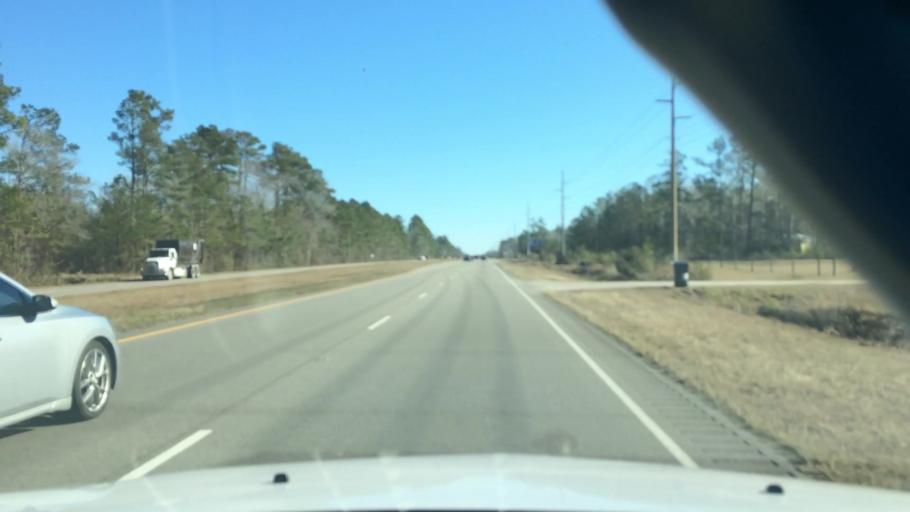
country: US
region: North Carolina
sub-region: Brunswick County
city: Shallotte
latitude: 34.0008
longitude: -78.3199
